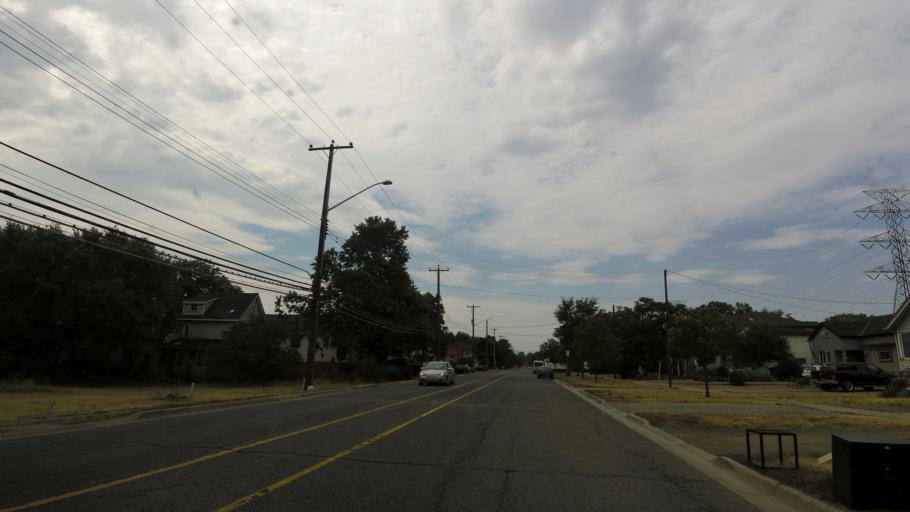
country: CA
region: Ontario
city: Hamilton
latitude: 43.2677
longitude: -79.7745
